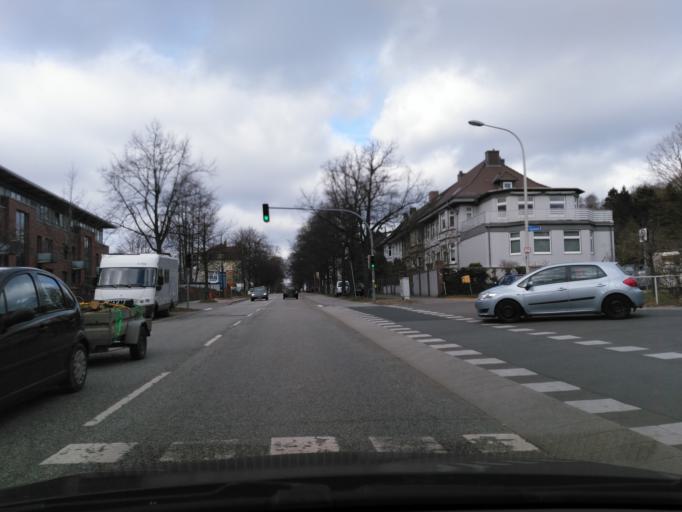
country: DE
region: Schleswig-Holstein
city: Kiel
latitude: 54.2968
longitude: 10.1046
